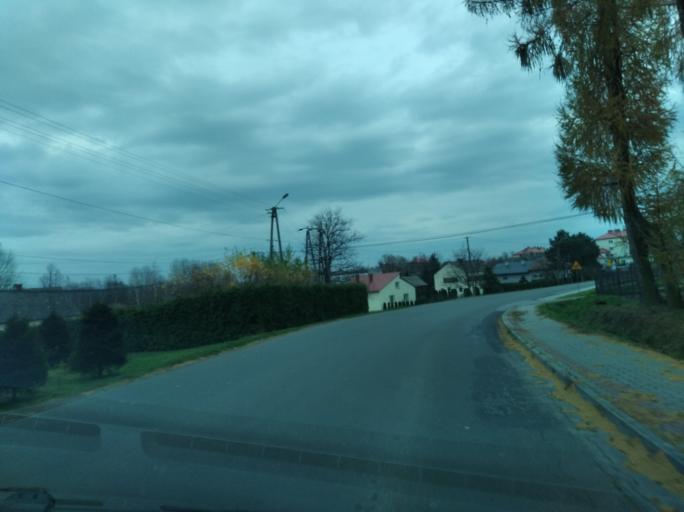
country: PL
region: Subcarpathian Voivodeship
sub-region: Powiat ropczycko-sedziszowski
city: Iwierzyce
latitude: 50.0304
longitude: 21.7547
